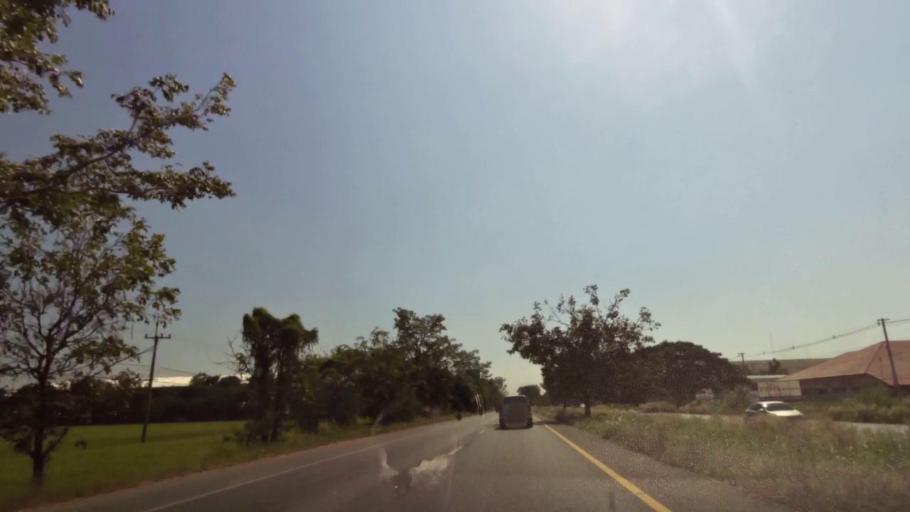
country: TH
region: Nakhon Sawan
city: Kao Liao
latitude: 15.8543
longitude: 100.1171
